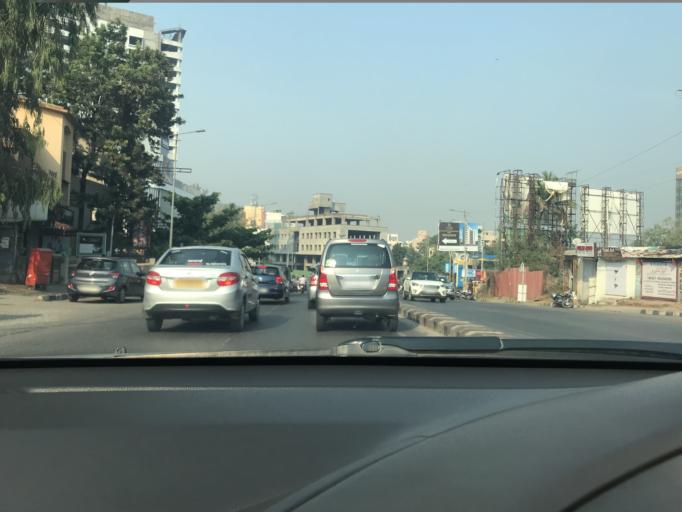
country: IN
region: Maharashtra
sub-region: Pune Division
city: Khadki
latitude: 18.5548
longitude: 73.8007
